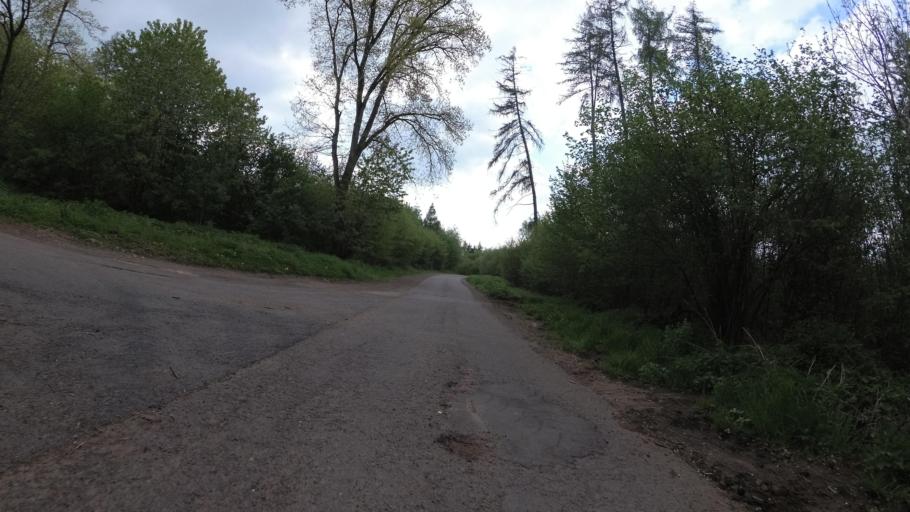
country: DE
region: Saarland
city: Marpingen
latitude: 49.4593
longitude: 7.0708
